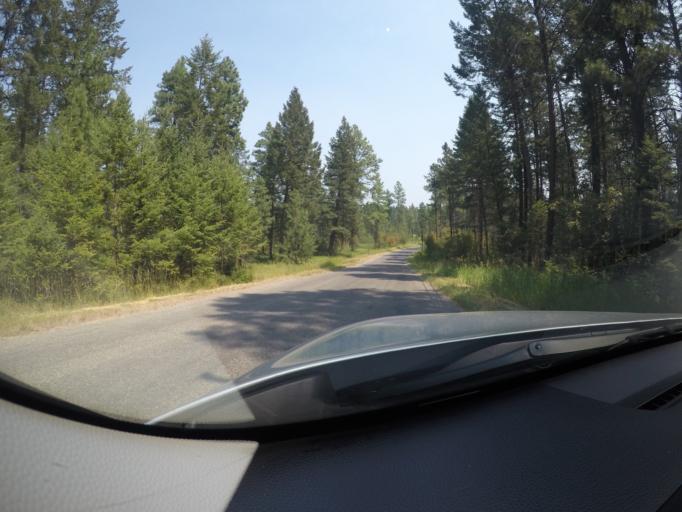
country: US
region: Montana
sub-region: Lake County
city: Polson
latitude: 47.7718
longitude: -114.1491
